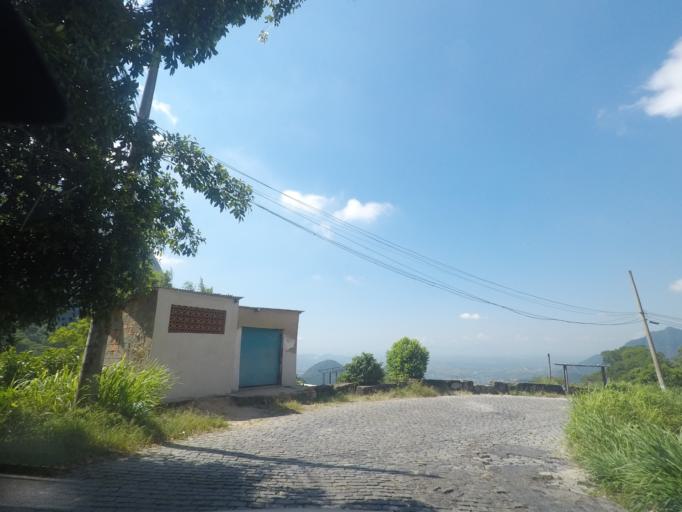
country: BR
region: Rio de Janeiro
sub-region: Petropolis
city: Petropolis
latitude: -22.5469
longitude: -43.1787
